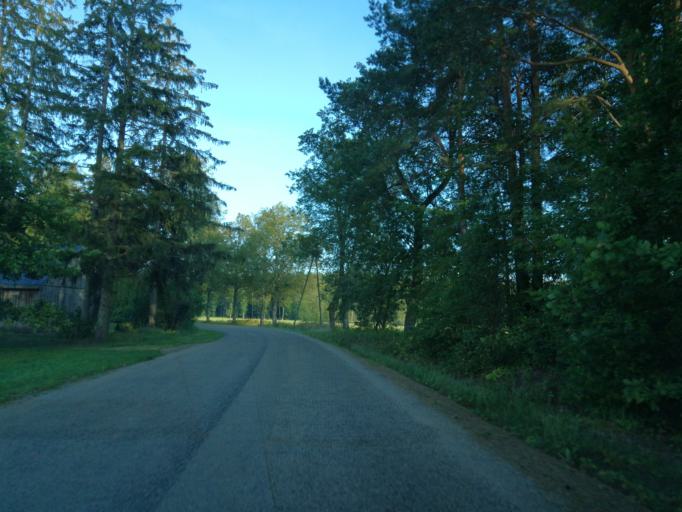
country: LV
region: Garkalne
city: Garkalne
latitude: 57.0766
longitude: 24.4562
